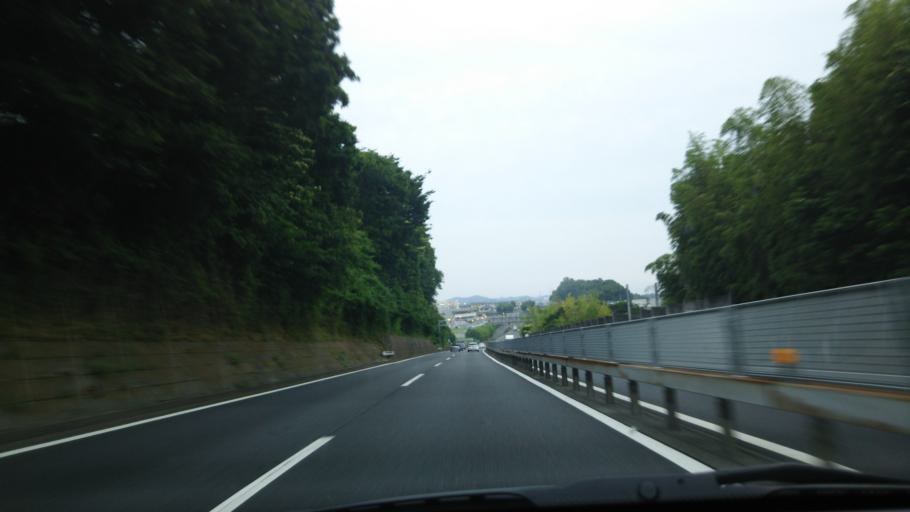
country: JP
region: Kanagawa
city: Oiso
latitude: 35.3439
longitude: 139.2967
